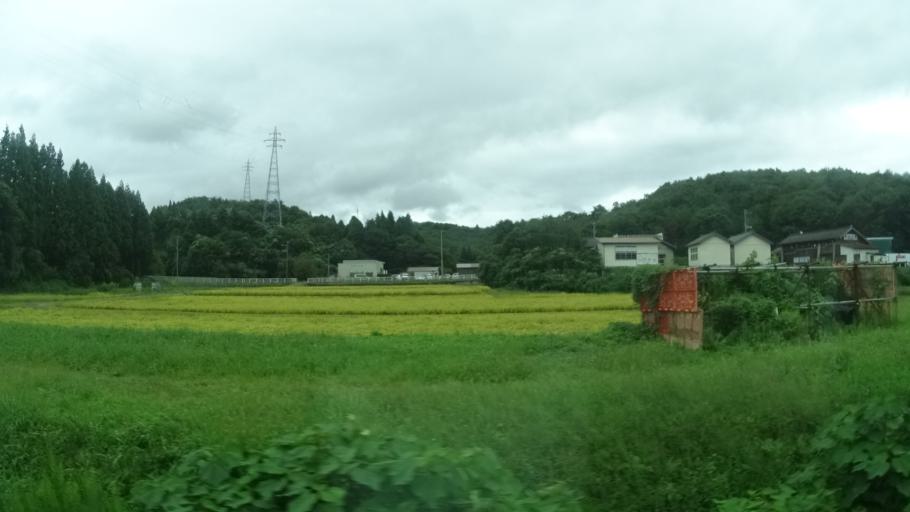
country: JP
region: Niigata
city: Murakami
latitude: 38.2112
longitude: 139.4621
